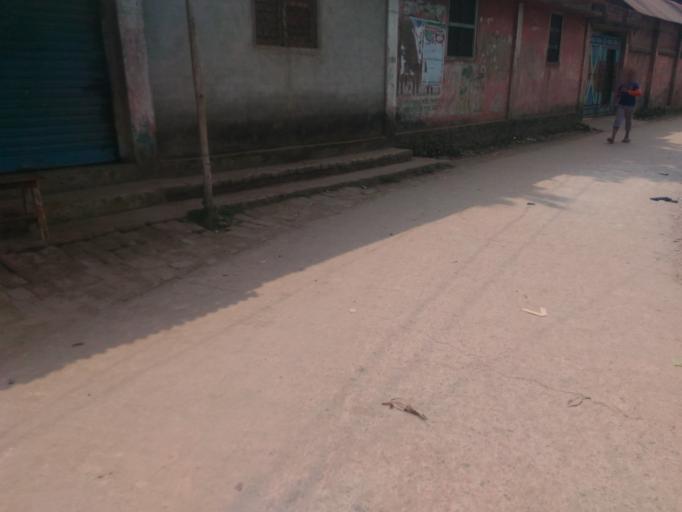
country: BD
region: Dhaka
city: Narayanganj
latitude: 23.6388
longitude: 90.4369
